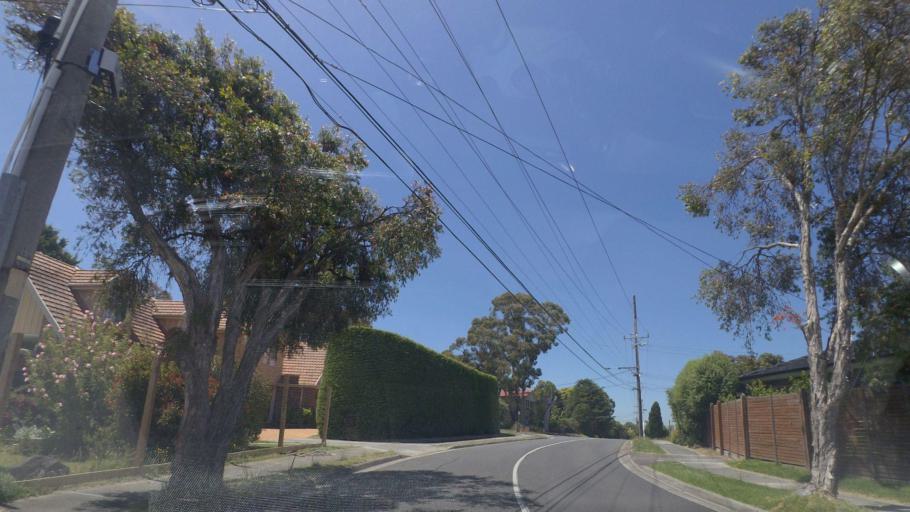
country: AU
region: Victoria
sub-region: Knox
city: Ferntree Gully
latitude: -37.8950
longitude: 145.2880
